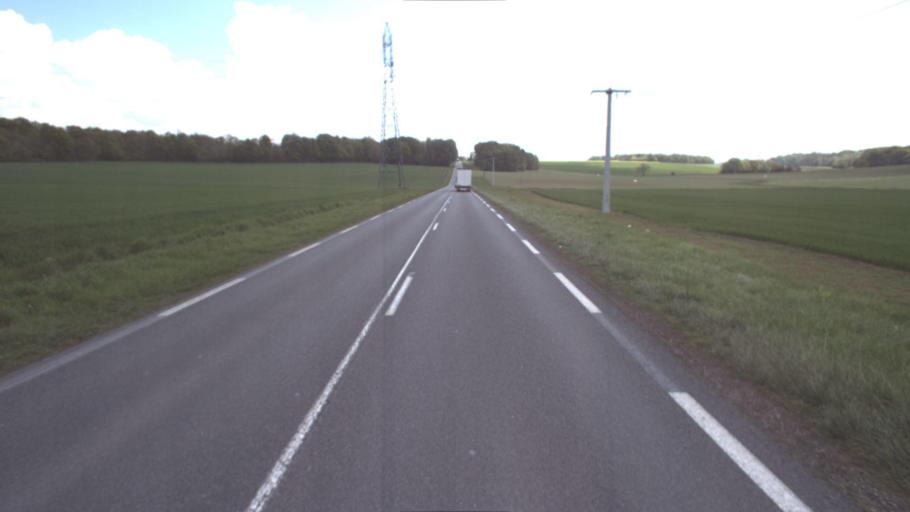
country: FR
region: Ile-de-France
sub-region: Departement de Seine-et-Marne
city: Jouy-le-Chatel
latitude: 48.6912
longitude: 3.1564
